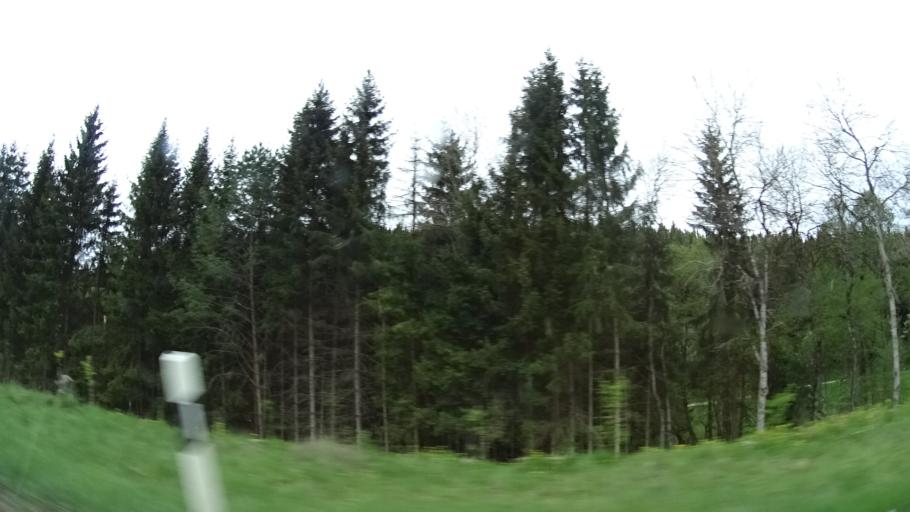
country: DE
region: Baden-Wuerttemberg
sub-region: Freiburg Region
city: Niedereschach
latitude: 48.1210
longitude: 8.5201
